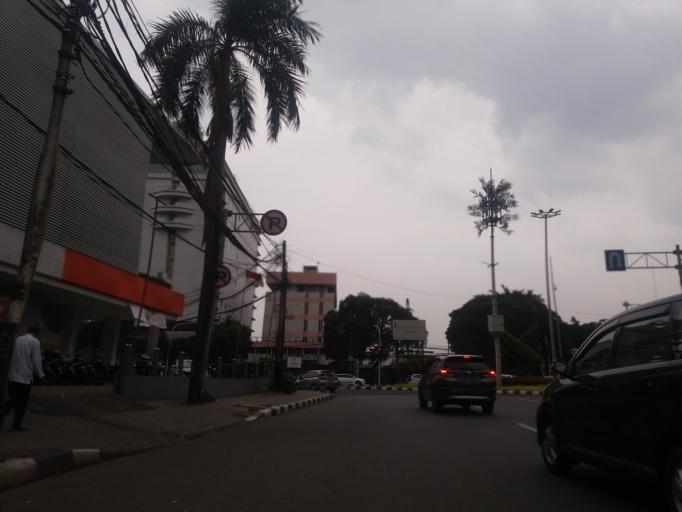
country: ID
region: Jakarta Raya
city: Jakarta
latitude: -6.1869
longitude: 106.8357
